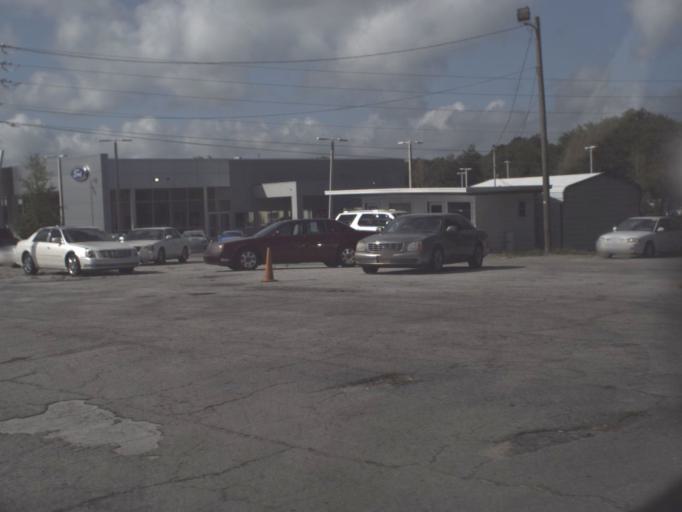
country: US
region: Florida
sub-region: Lake County
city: Leesburg
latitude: 28.8364
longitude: -81.8911
